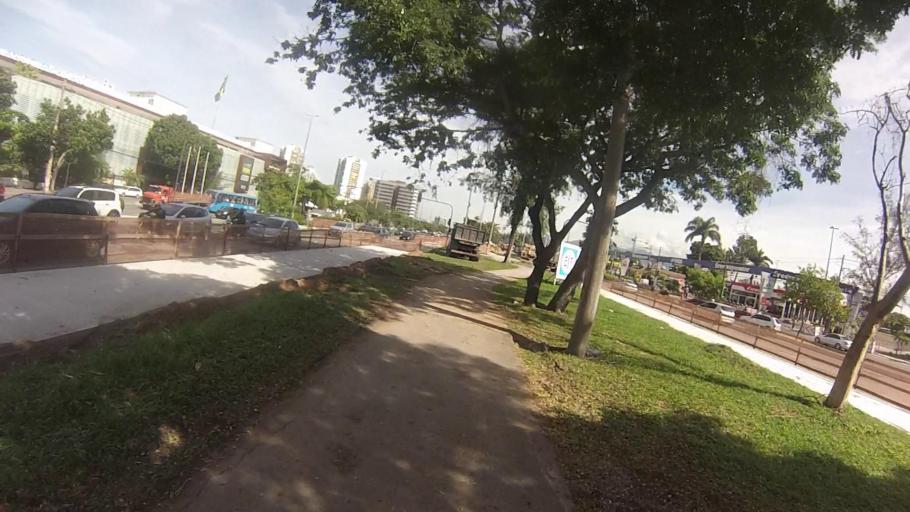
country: BR
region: Rio de Janeiro
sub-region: Rio De Janeiro
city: Rio de Janeiro
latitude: -23.0006
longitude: -43.3344
